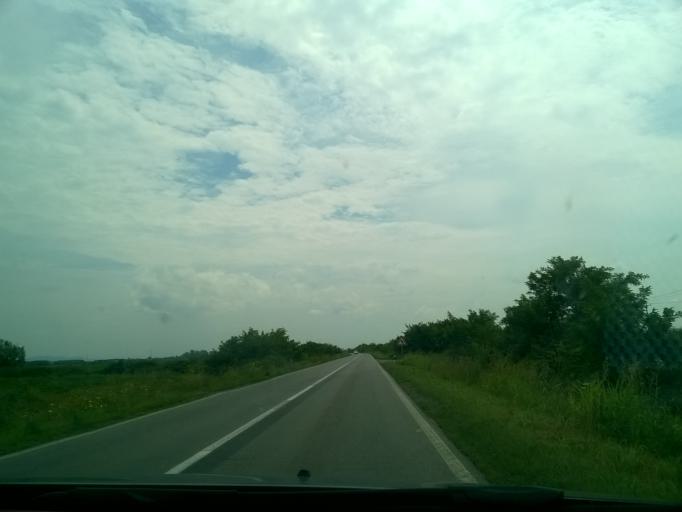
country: RS
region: Autonomna Pokrajina Vojvodina
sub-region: Juznobanatski Okrug
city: Plandiste
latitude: 45.2501
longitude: 21.1015
